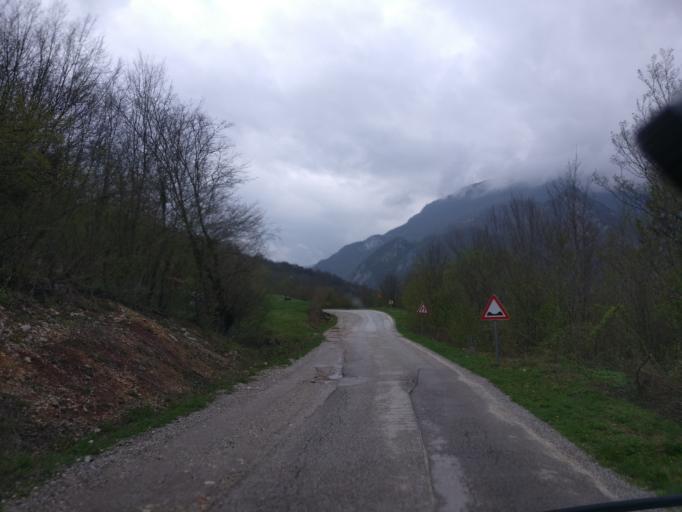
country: BA
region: Republika Srpska
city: Foca
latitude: 43.3517
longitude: 18.8295
